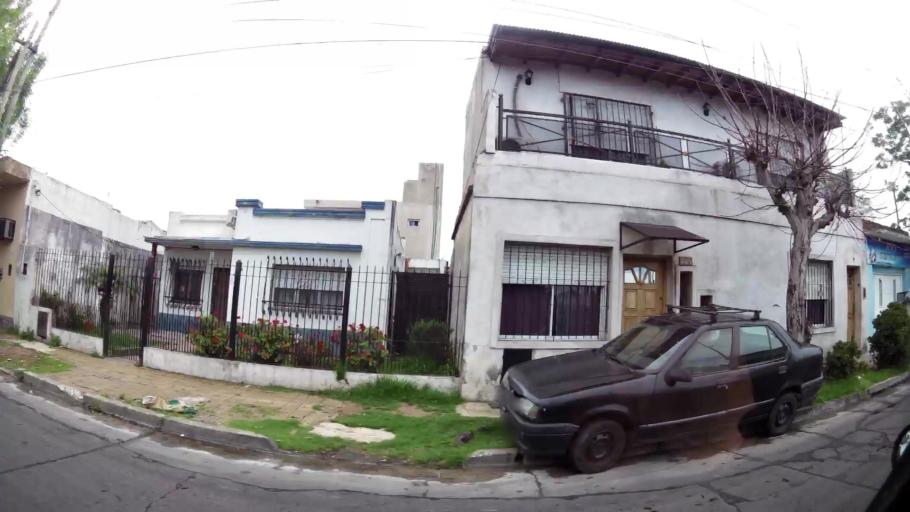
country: AR
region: Buenos Aires
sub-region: Partido de Quilmes
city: Quilmes
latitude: -34.7560
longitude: -58.2194
